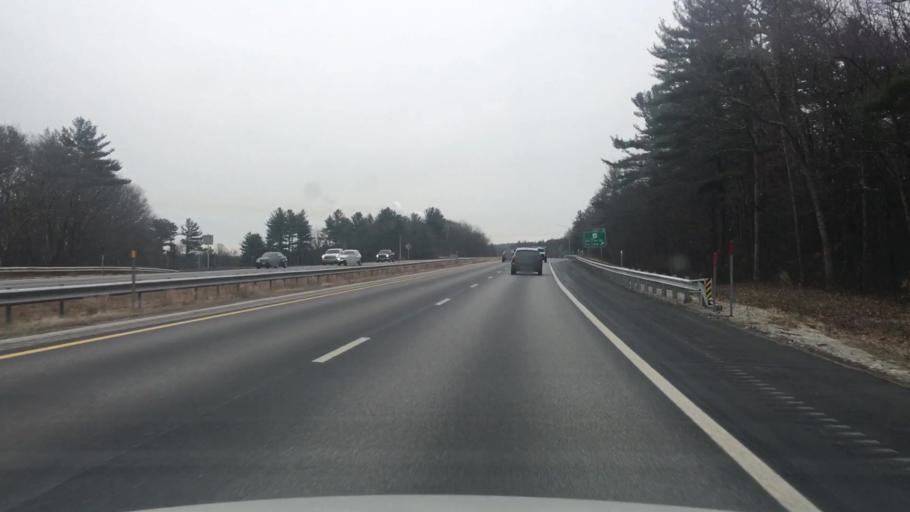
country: US
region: New Hampshire
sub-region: Merrimack County
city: Concord
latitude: 43.1813
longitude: -71.5700
